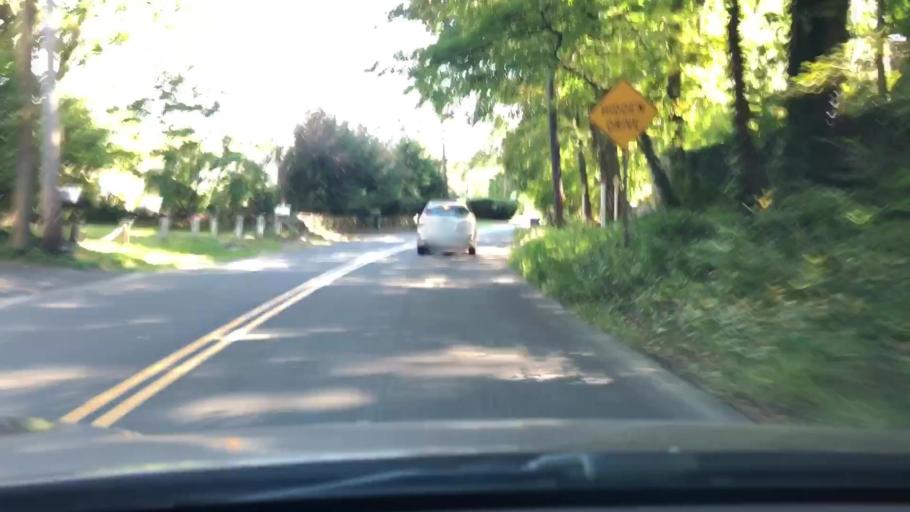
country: US
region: Connecticut
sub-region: Fairfield County
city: Darien
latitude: 41.1093
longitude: -73.4634
